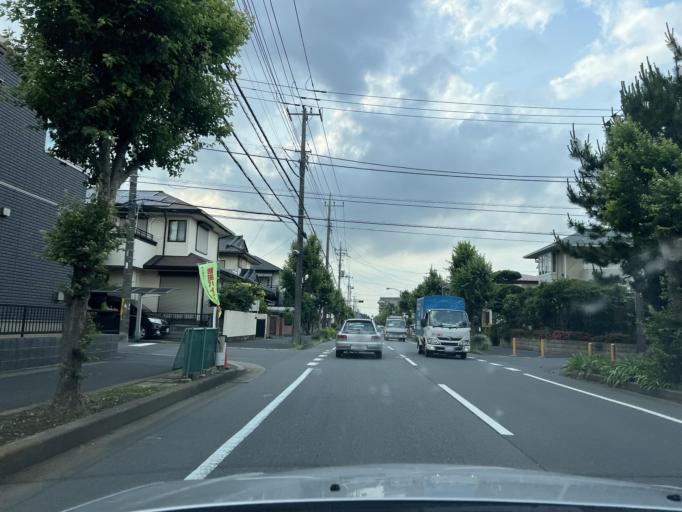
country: JP
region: Chiba
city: Nagareyama
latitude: 35.8796
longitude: 139.9151
